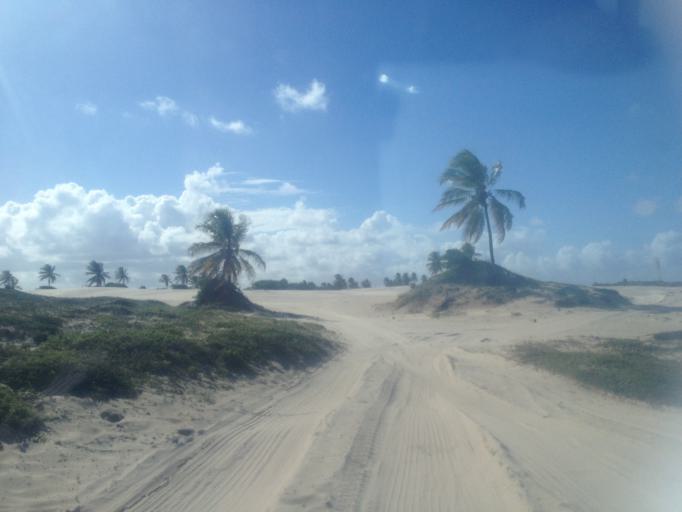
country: BR
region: Sergipe
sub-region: Indiaroba
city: Indiaroba
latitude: -11.4692
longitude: -37.3675
